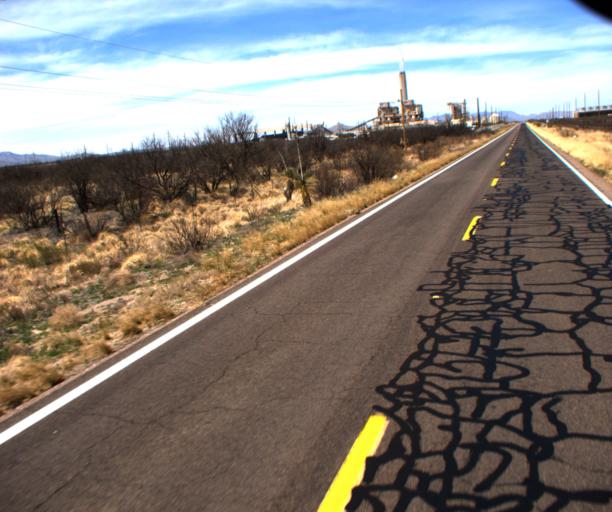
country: US
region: Arizona
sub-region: Cochise County
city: Willcox
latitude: 32.0521
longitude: -109.8871
